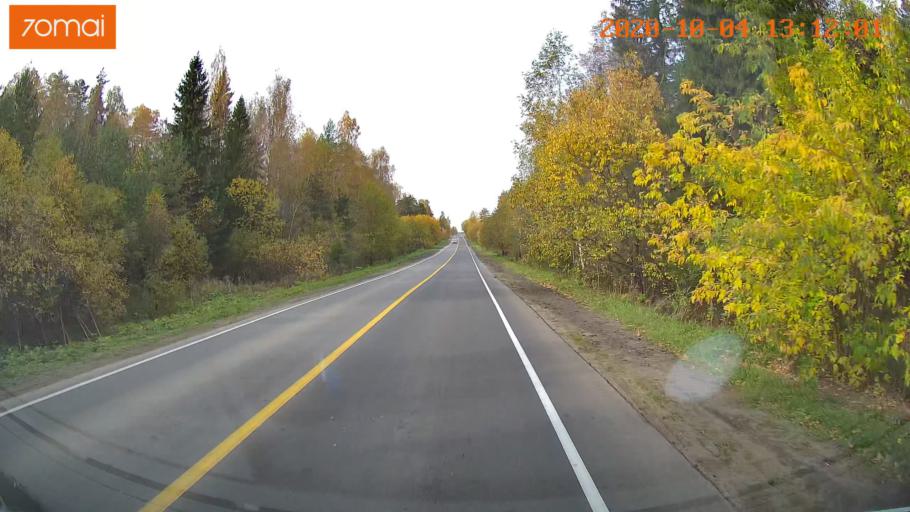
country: RU
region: Ivanovo
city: Bogorodskoye
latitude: 57.0808
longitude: 40.9337
